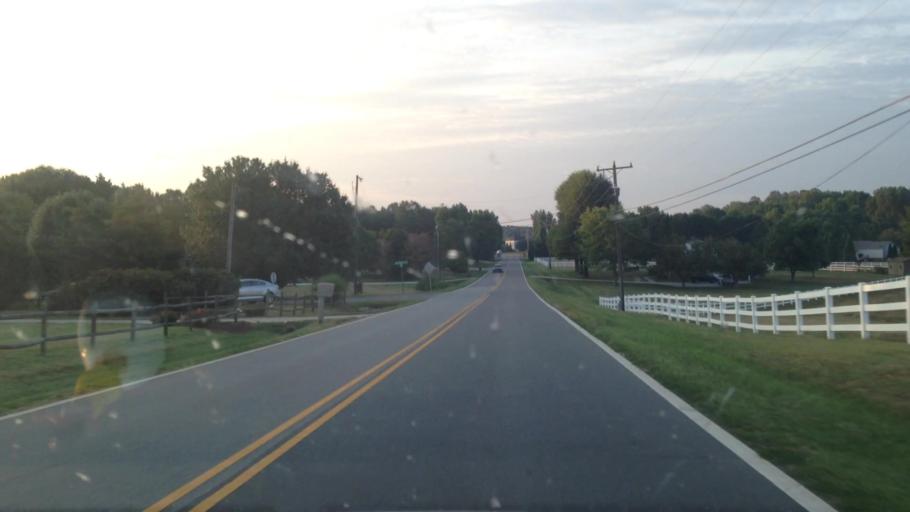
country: US
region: North Carolina
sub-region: Forsyth County
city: Kernersville
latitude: 36.1464
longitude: -80.0865
